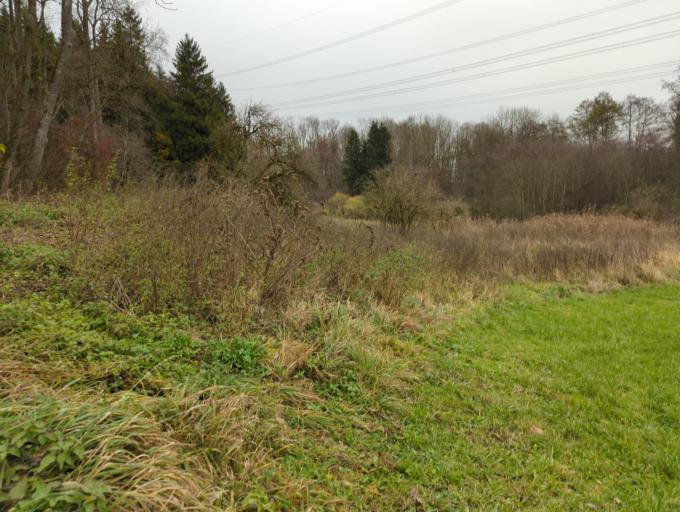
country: DE
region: Bavaria
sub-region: Swabia
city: Guenzburg
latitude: 48.4390
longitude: 10.3080
